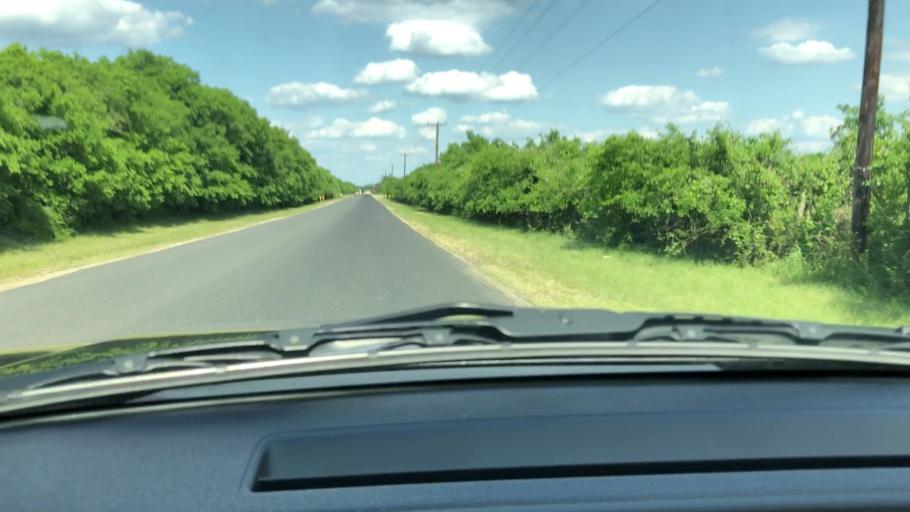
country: US
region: Texas
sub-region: Bexar County
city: Timberwood Park
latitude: 29.7307
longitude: -98.5090
